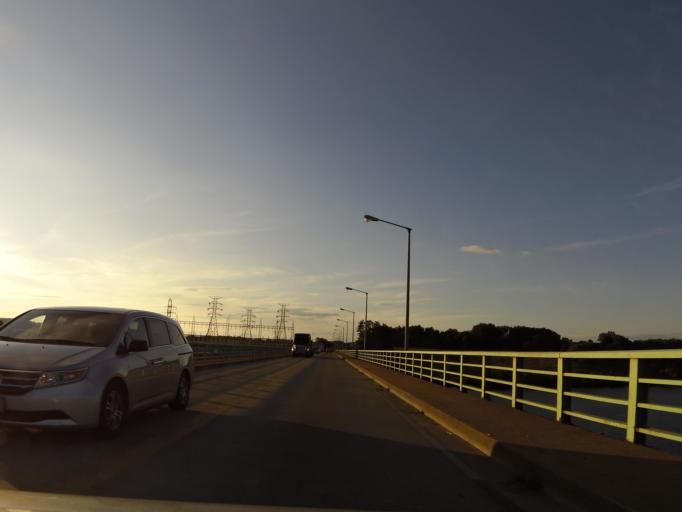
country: US
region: Tennessee
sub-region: Loudon County
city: Lenoir City
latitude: 35.7902
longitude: -84.2422
